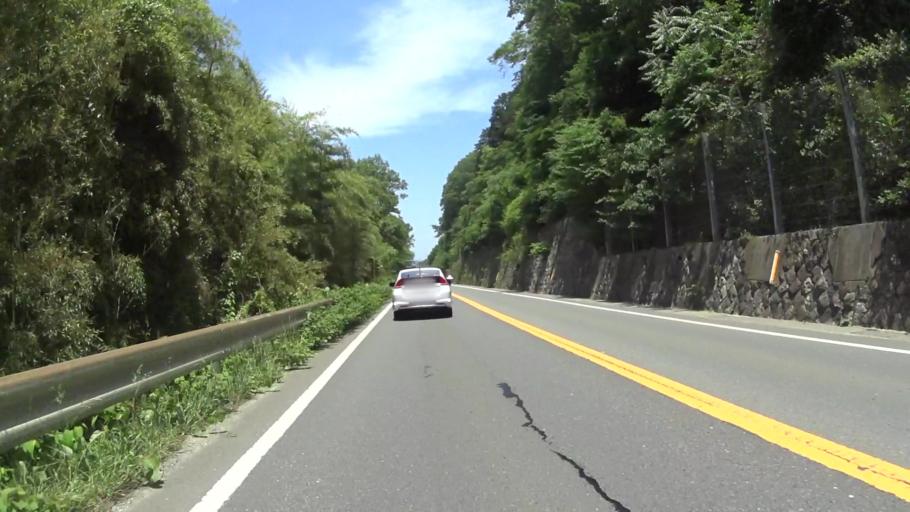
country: JP
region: Kyoto
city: Kameoka
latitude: 35.1443
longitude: 135.4270
